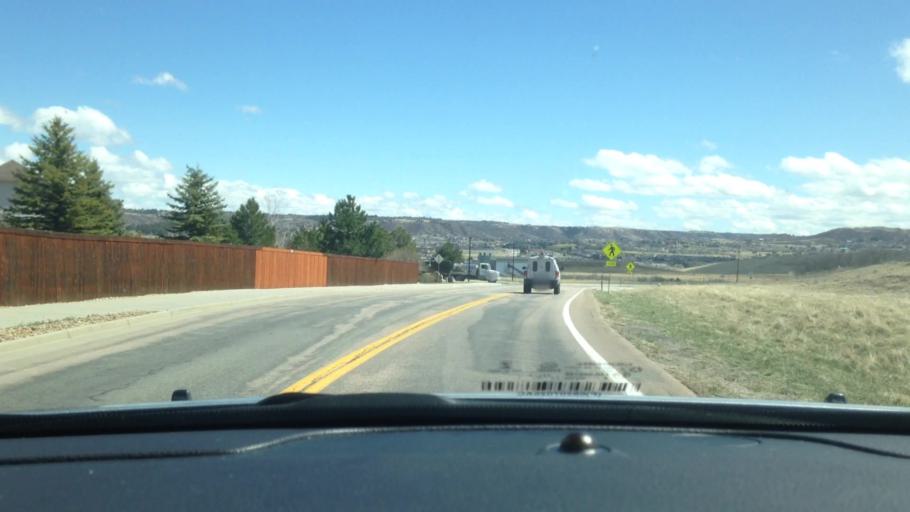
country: US
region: Colorado
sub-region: Douglas County
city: Castle Rock
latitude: 39.3743
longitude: -104.8790
